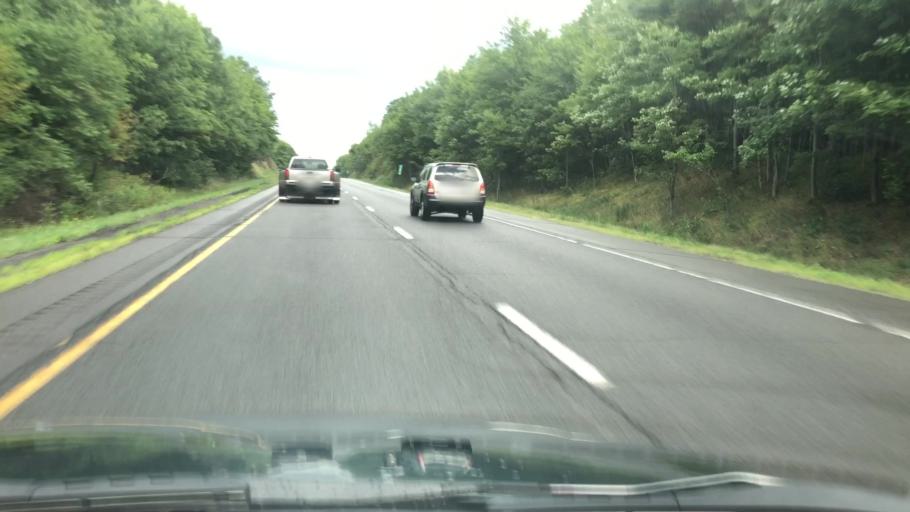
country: US
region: Pennsylvania
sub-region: Wayne County
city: Hawley
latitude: 41.3612
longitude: -75.1632
